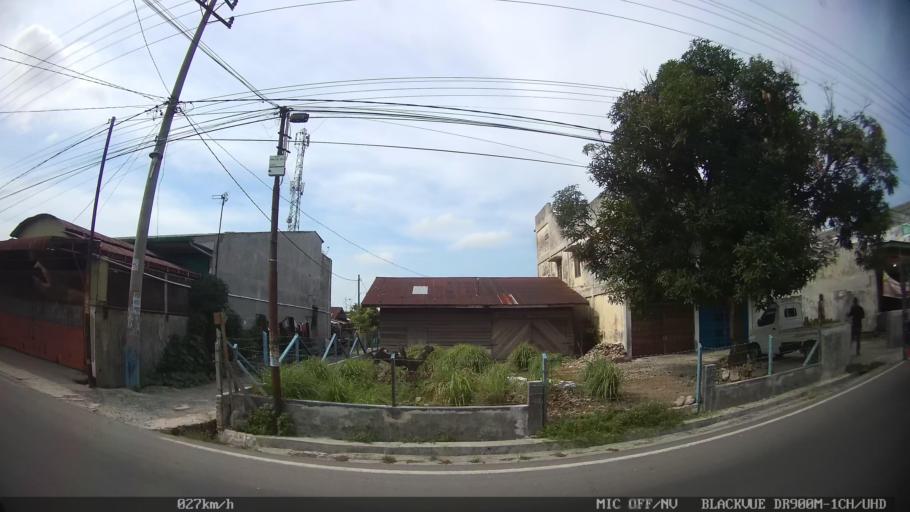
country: ID
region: North Sumatra
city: Percut
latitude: 3.6073
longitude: 98.7683
